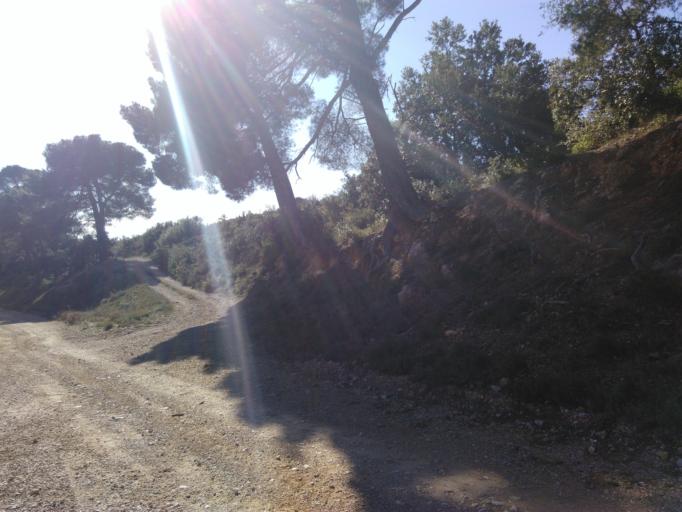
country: FR
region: Provence-Alpes-Cote d'Azur
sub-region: Departement du Vaucluse
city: Beaumes-de-Venise
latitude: 44.1389
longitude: 5.0194
